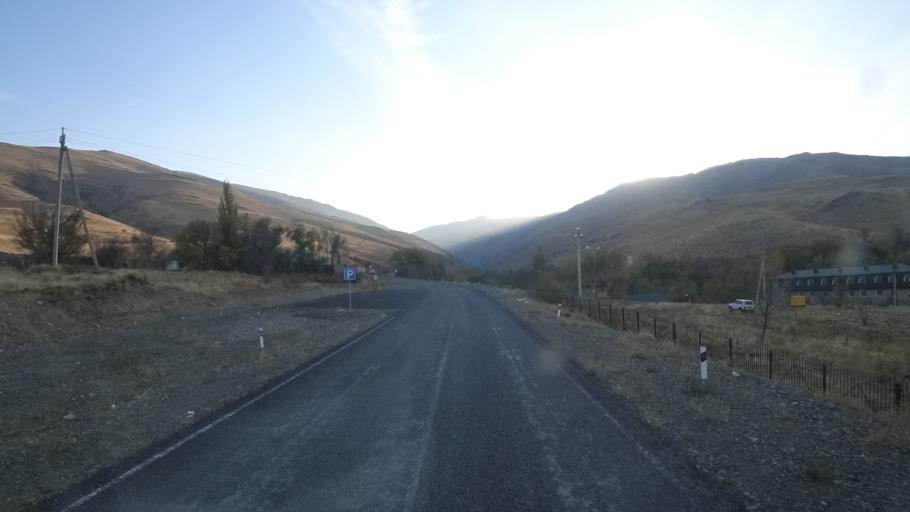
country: KZ
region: Zhambyl
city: Karatau
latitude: 42.9278
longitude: 70.6462
